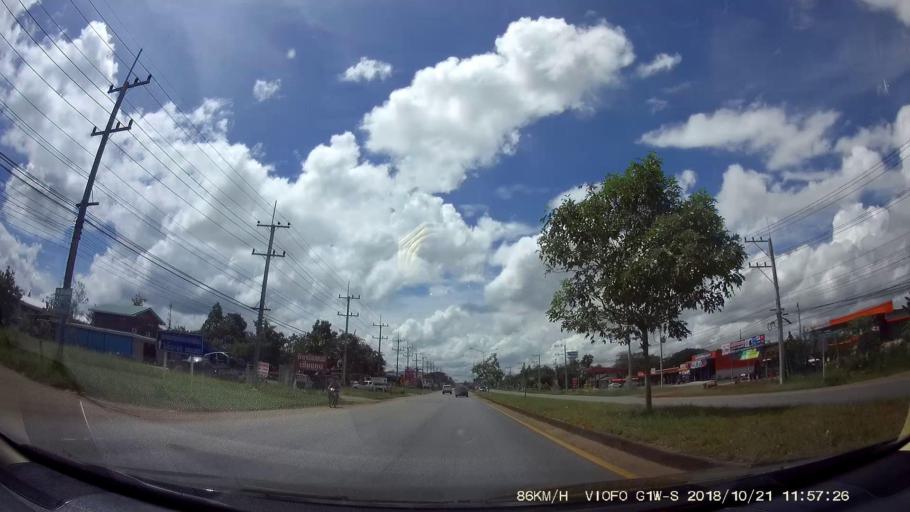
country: TH
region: Chaiyaphum
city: Chatturat
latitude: 15.5754
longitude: 101.8635
